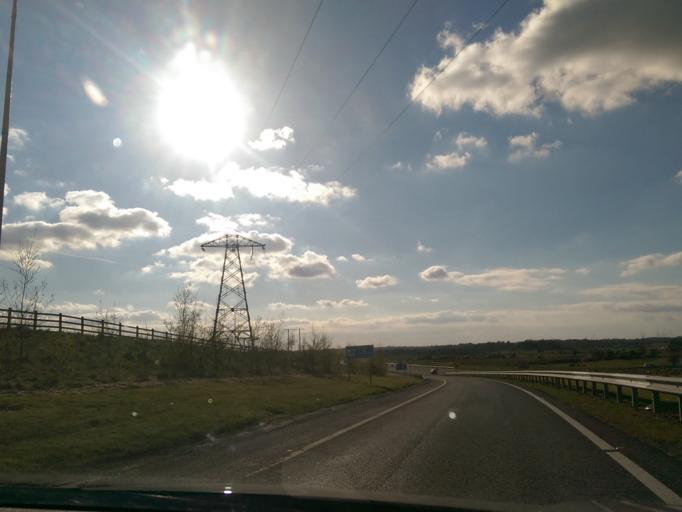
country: IE
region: Connaught
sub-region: County Galway
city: Loughrea
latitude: 53.2645
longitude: -8.6099
